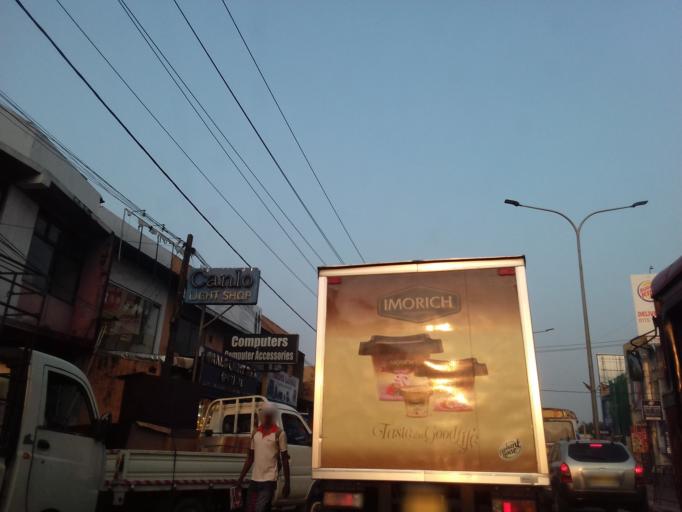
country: LK
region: Western
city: Kelaniya
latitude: 6.9741
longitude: 79.9221
